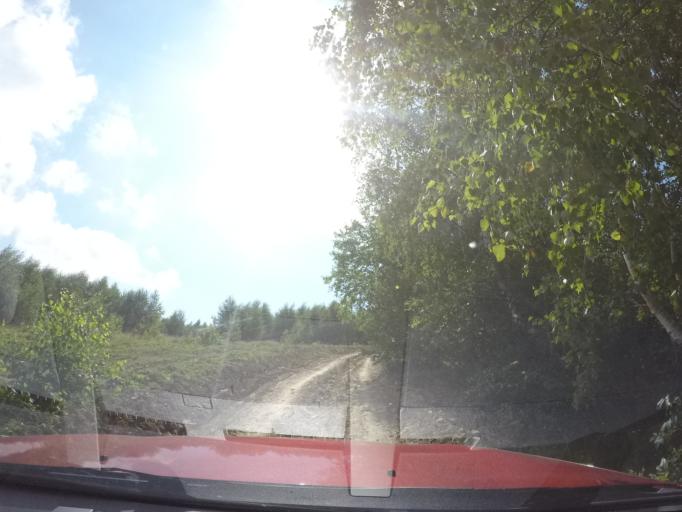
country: UA
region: Zakarpattia
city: Velykyi Bereznyi
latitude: 48.9477
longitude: 22.6662
